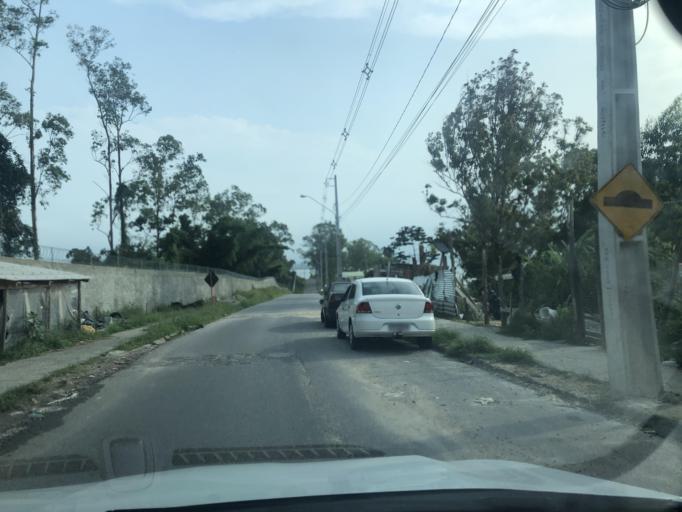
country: BR
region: Santa Catarina
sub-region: Florianopolis
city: Carvoeira
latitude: -27.5993
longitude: -48.5326
